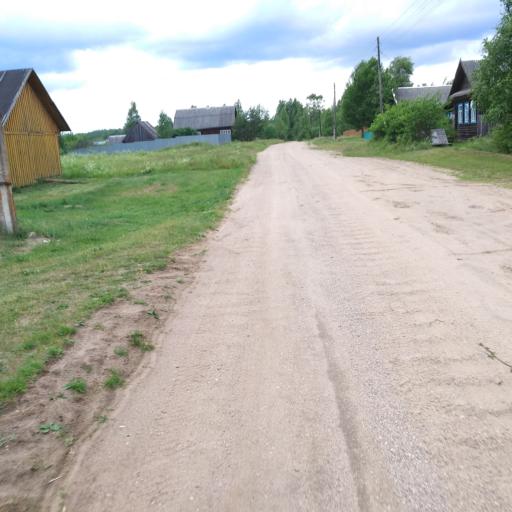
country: RU
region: Tverskaya
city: Krasnomayskiy
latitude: 57.5358
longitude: 34.3432
